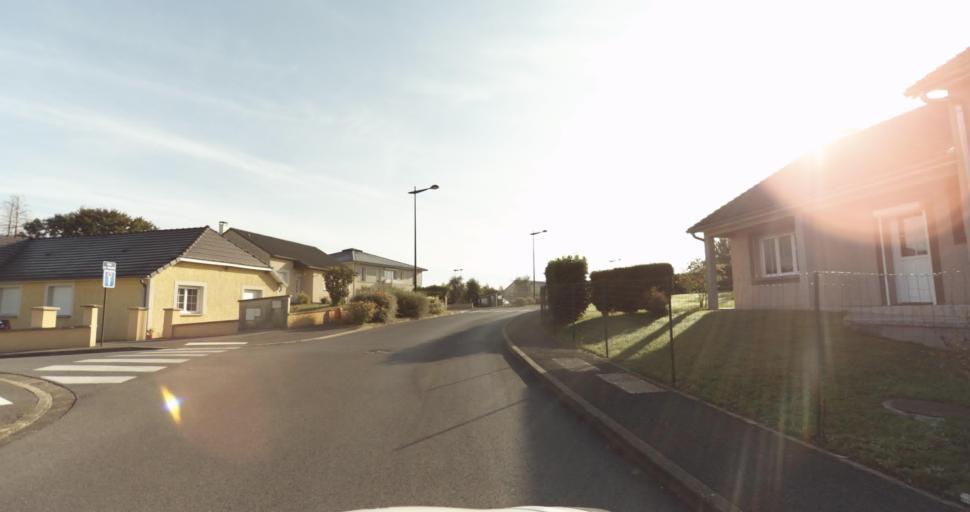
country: FR
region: Champagne-Ardenne
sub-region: Departement des Ardennes
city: Villers-Semeuse
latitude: 49.7399
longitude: 4.7423
